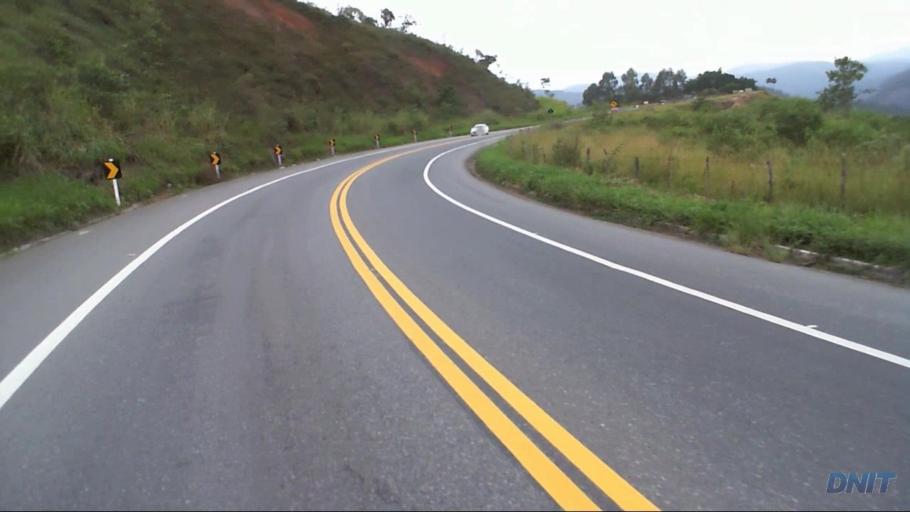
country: BR
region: Minas Gerais
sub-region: Nova Era
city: Nova Era
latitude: -19.6844
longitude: -42.9861
